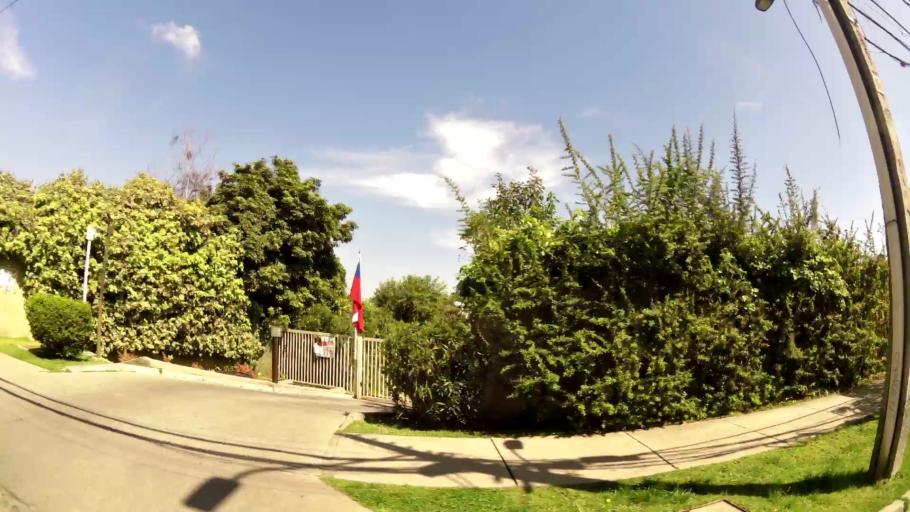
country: CL
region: Santiago Metropolitan
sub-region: Provincia de Santiago
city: Villa Presidente Frei, Nunoa, Santiago, Chile
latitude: -33.4449
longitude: -70.5235
